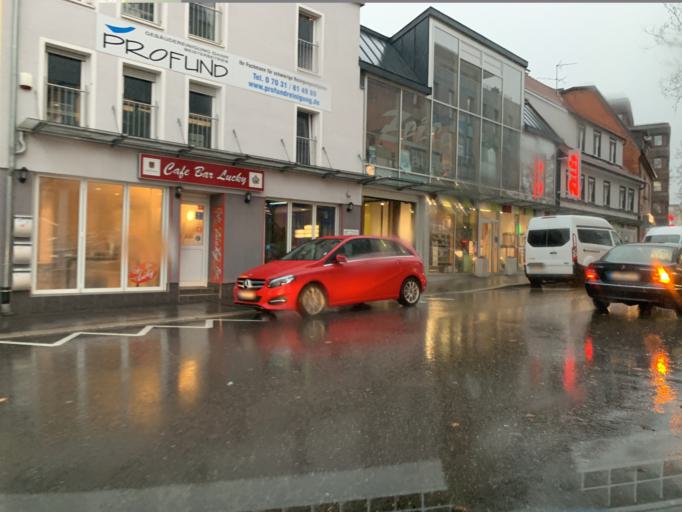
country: DE
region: Baden-Wuerttemberg
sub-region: Regierungsbezirk Stuttgart
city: Sindelfingen
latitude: 48.7075
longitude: 8.9985
